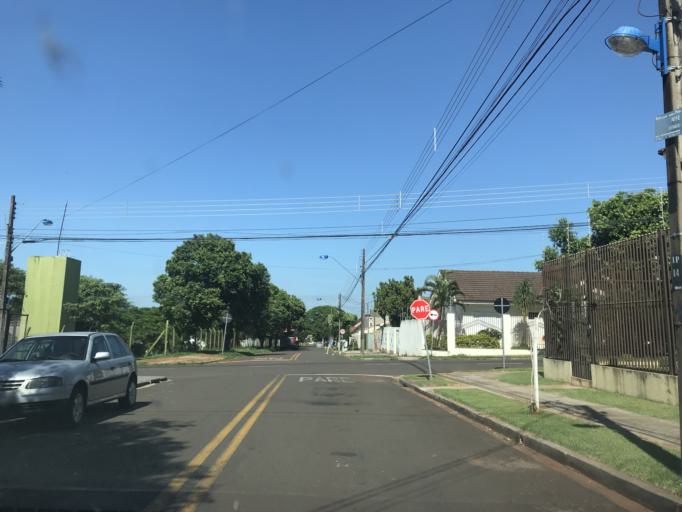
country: BR
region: Parana
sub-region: Maringa
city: Maringa
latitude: -23.4492
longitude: -51.9589
